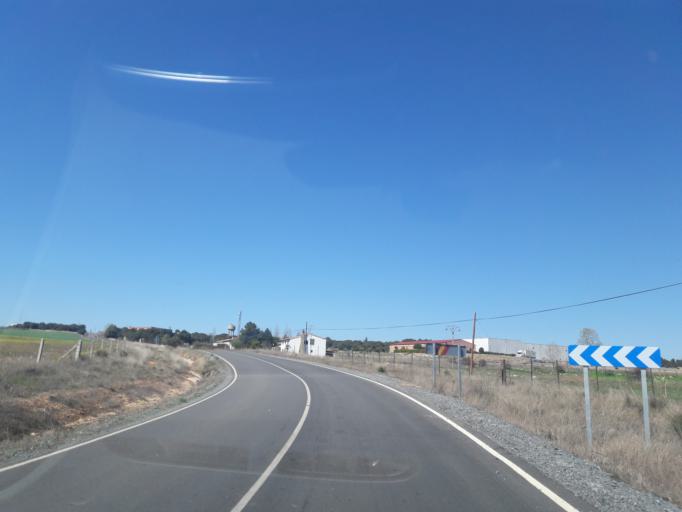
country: ES
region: Castille and Leon
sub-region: Provincia de Salamanca
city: Martinamor
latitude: 40.8105
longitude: -5.6230
